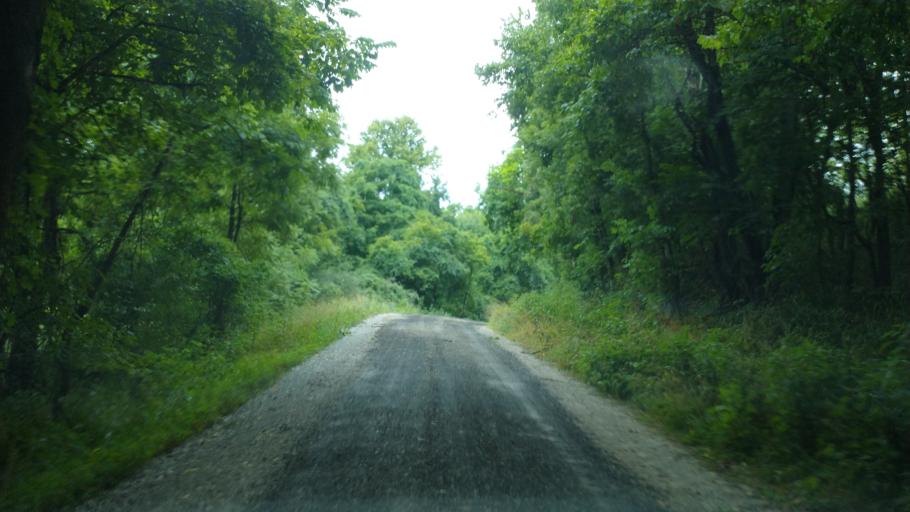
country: US
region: Ohio
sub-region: Meigs County
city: Middleport
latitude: 38.9304
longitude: -82.0681
